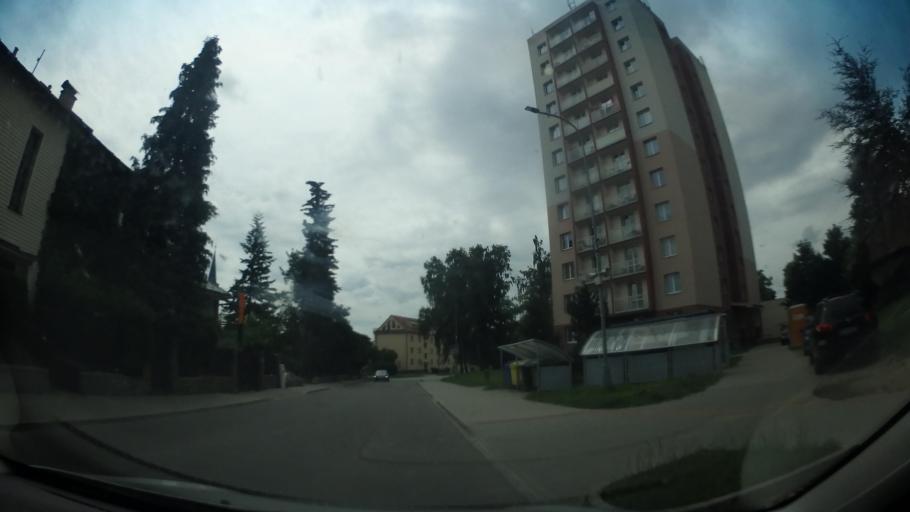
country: CZ
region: Vysocina
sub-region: Okres Zd'ar nad Sazavou
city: Nove Mesto na Morave
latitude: 49.5650
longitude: 16.0749
